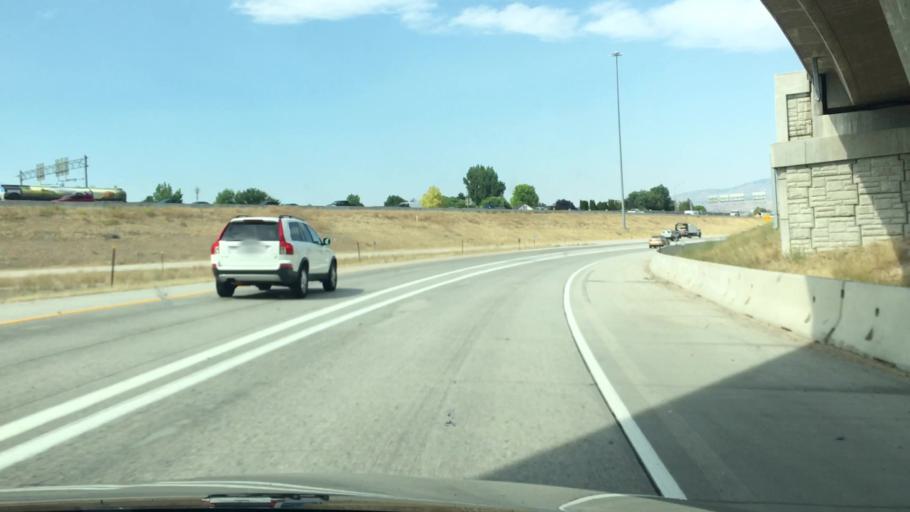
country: US
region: Idaho
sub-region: Ada County
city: Garden City
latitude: 43.5985
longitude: -116.2860
